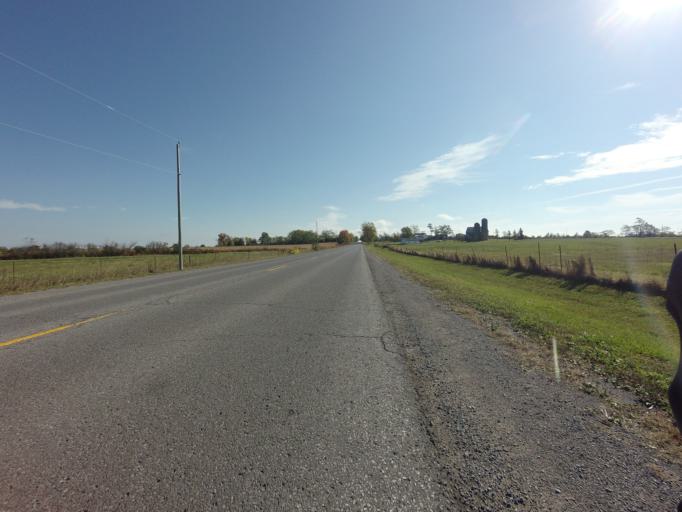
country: CA
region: Ontario
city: Prince Edward
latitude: 44.0151
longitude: -77.3131
